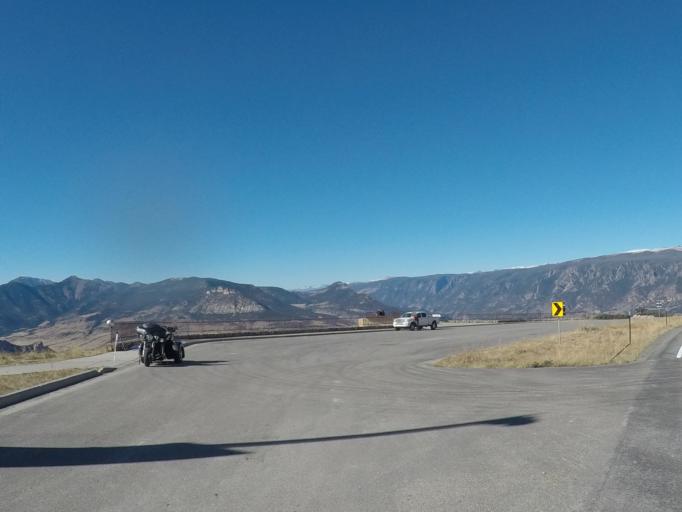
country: US
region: Wyoming
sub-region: Park County
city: Cody
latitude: 44.7436
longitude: -109.3840
